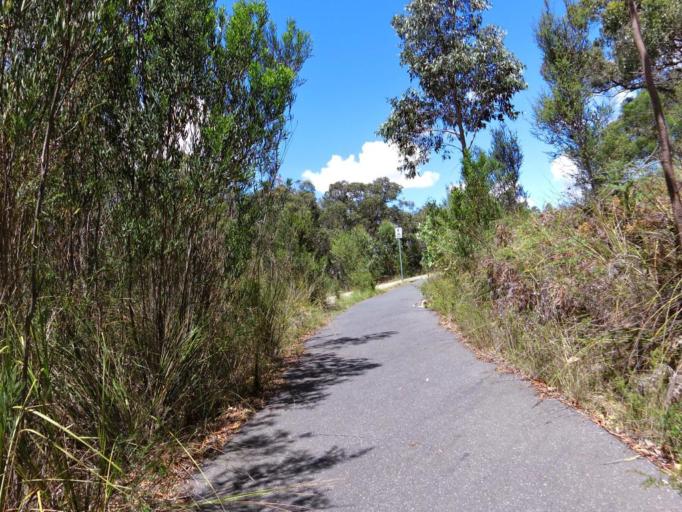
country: AU
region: Victoria
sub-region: Cardinia
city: Officer
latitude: -38.0314
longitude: 145.4278
